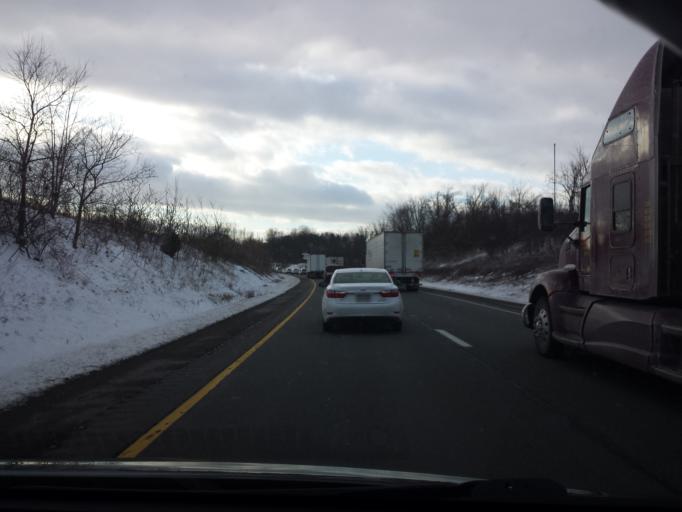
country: US
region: Pennsylvania
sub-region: Columbia County
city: Almedia
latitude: 41.0392
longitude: -76.3570
